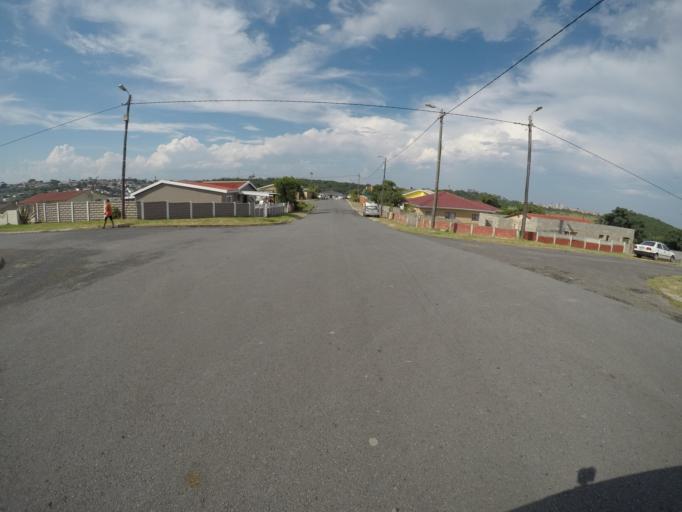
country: ZA
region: Eastern Cape
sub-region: Buffalo City Metropolitan Municipality
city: East London
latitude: -33.0225
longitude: 27.8809
